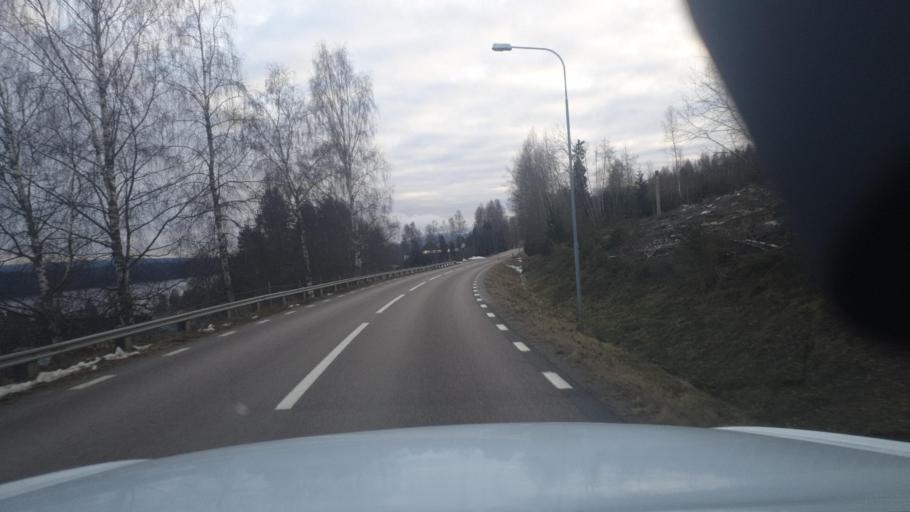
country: SE
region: Vaermland
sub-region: Sunne Kommun
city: Sunne
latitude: 59.8757
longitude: 12.9356
